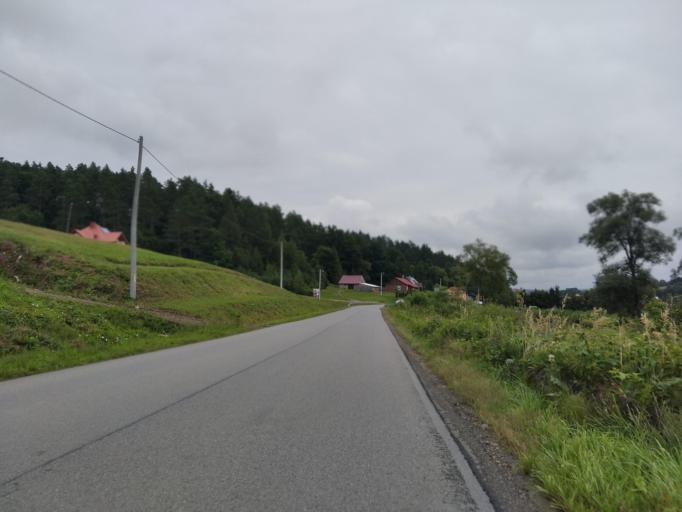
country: PL
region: Subcarpathian Voivodeship
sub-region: Powiat przemyski
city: Bircza
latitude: 49.6976
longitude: 22.3798
